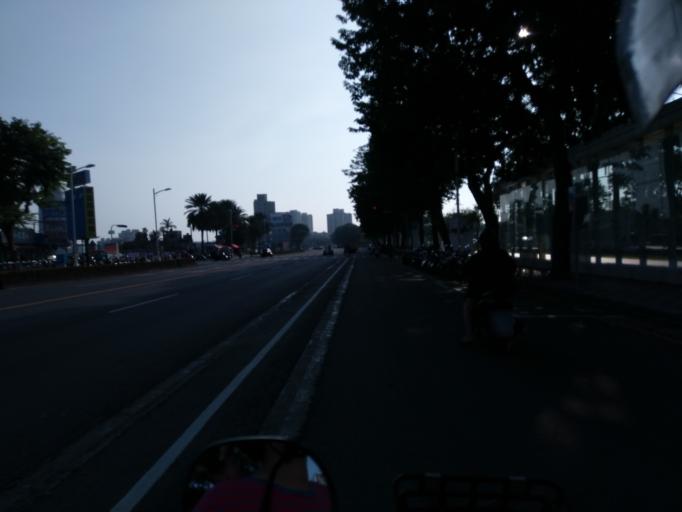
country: TW
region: Kaohsiung
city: Kaohsiung
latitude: 22.5996
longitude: 120.3200
